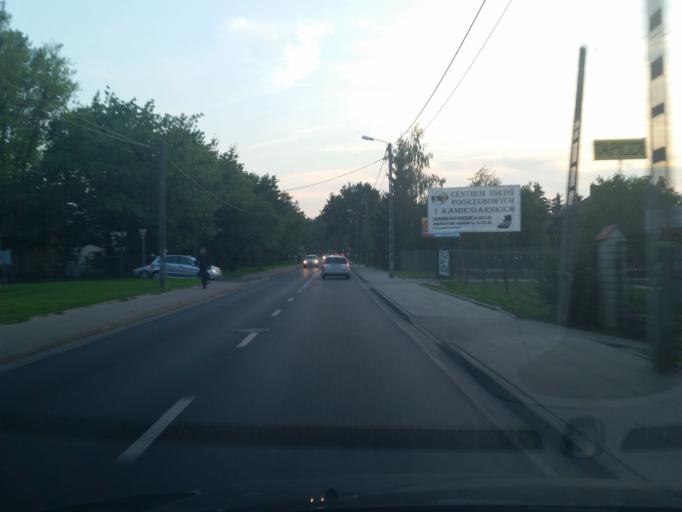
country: PL
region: Masovian Voivodeship
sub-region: Warszawa
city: Bialoleka
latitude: 52.3339
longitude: 20.9601
